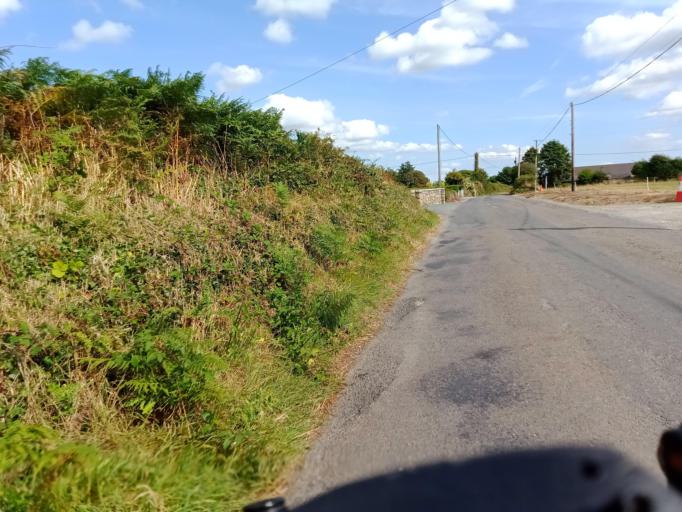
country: IE
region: Munster
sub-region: Waterford
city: Dungarvan
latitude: 52.1189
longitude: -7.4902
